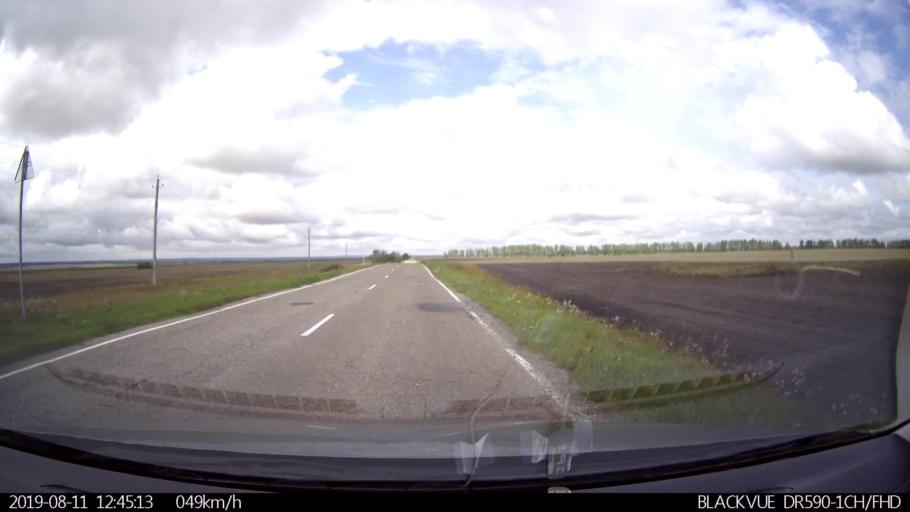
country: RU
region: Ulyanovsk
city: Ignatovka
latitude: 53.8584
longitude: 47.7298
